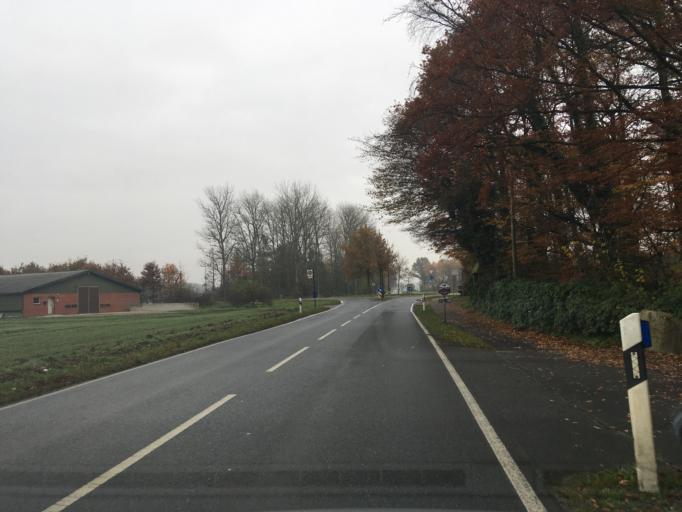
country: DE
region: North Rhine-Westphalia
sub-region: Regierungsbezirk Munster
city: Gescher
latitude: 52.0068
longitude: 7.0336
